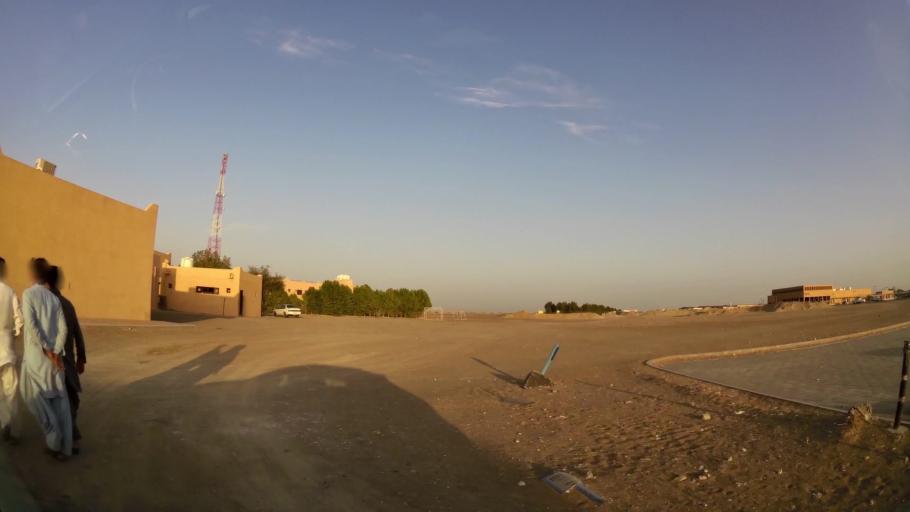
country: AE
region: Abu Dhabi
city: Al Ain
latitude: 24.1624
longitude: 55.8173
